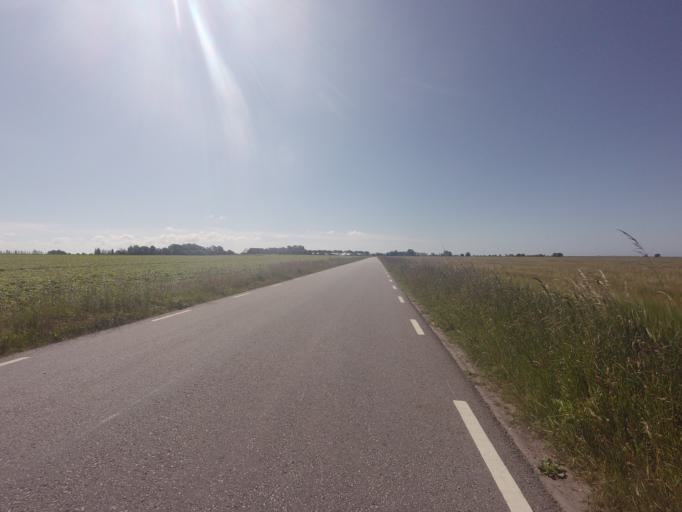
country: SE
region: Skane
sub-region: Malmo
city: Bunkeflostrand
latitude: 55.5182
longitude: 12.9341
